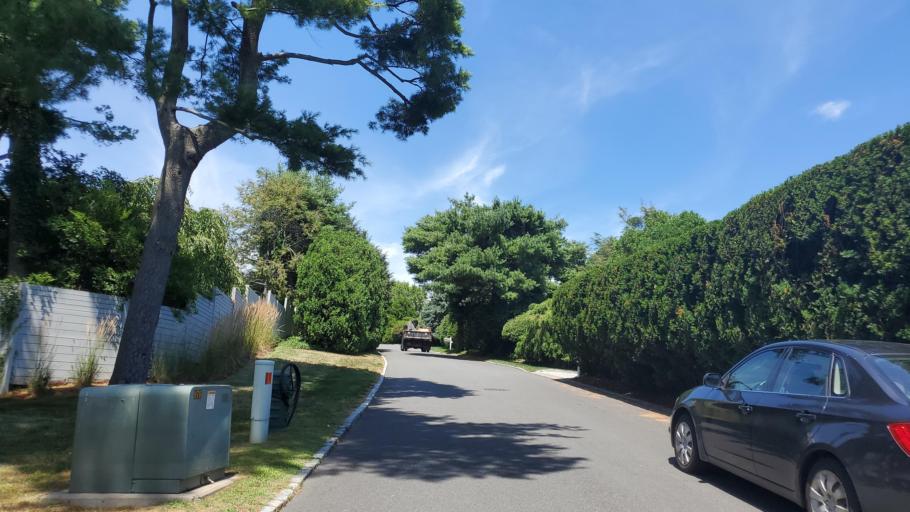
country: US
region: Connecticut
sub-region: Fairfield County
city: Westport
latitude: 41.1109
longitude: -73.3493
